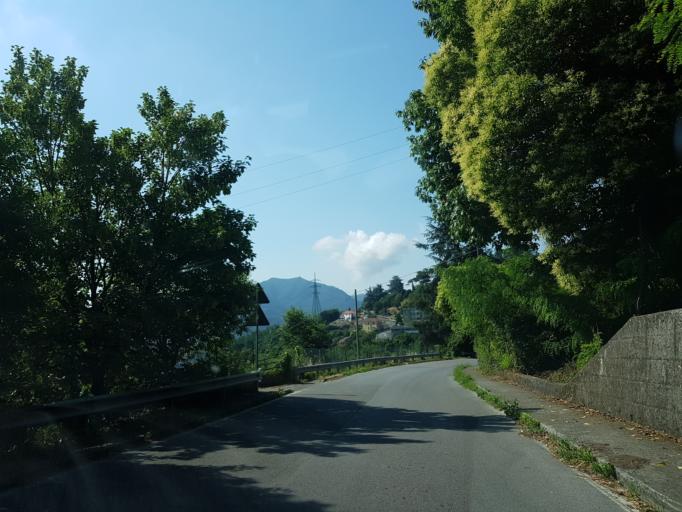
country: IT
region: Liguria
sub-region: Provincia di Genova
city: Pedemonte
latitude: 44.4978
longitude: 8.9132
